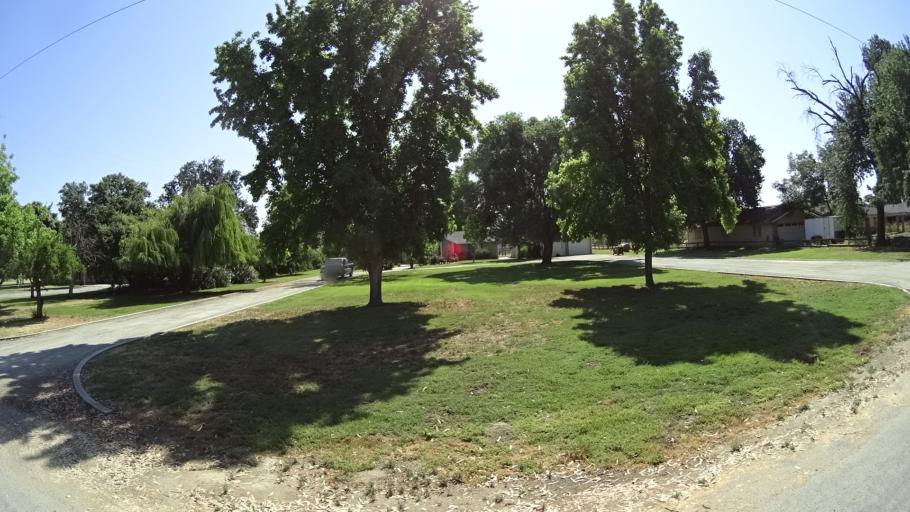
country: US
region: California
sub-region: Kings County
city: Lemoore
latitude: 36.3543
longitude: -119.8250
